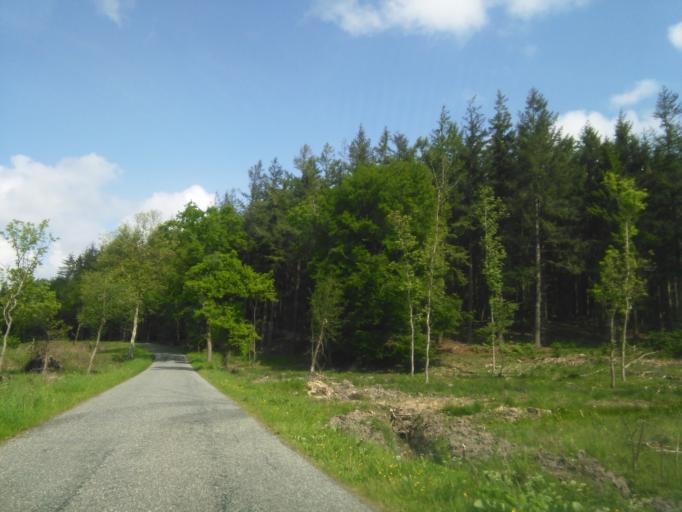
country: DK
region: Central Jutland
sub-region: Skanderborg Kommune
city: Galten
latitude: 56.2216
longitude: 9.9296
